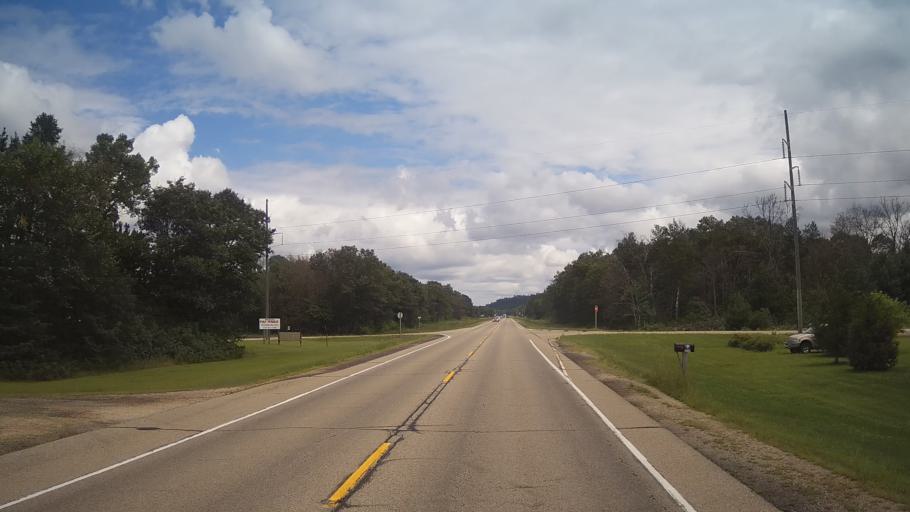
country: US
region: Wisconsin
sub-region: Juneau County
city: New Lisbon
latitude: 44.0322
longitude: -90.0462
